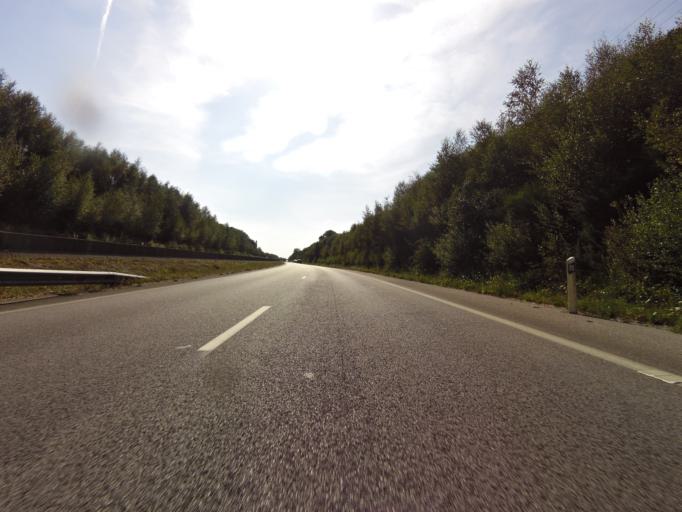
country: FR
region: Brittany
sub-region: Departement du Finistere
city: Quimper
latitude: 48.0029
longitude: -4.1403
